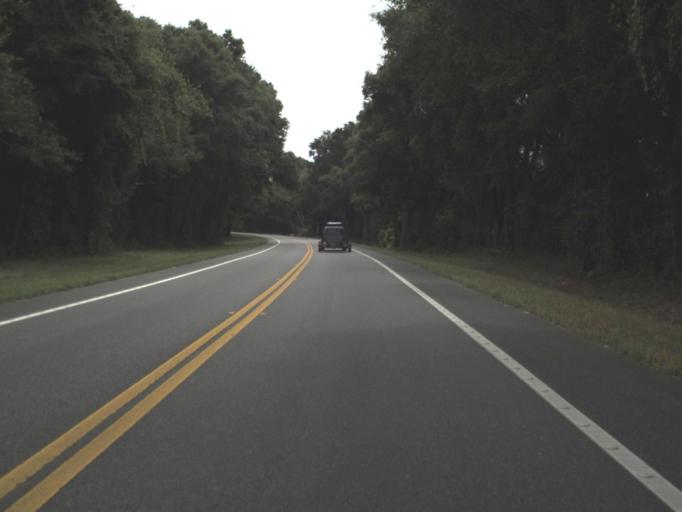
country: US
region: Florida
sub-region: Suwannee County
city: Wellborn
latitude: 29.9723
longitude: -82.8911
